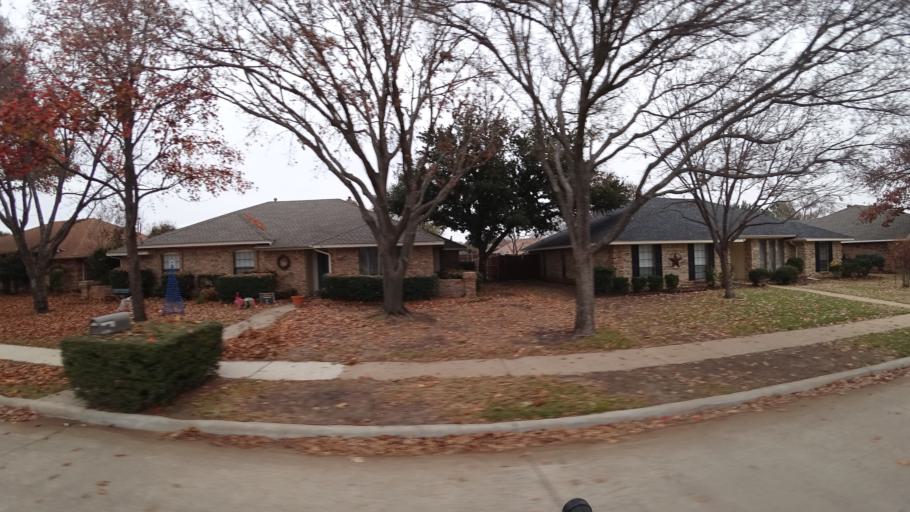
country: US
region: Texas
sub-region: Denton County
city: Highland Village
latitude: 33.0567
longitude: -97.0432
